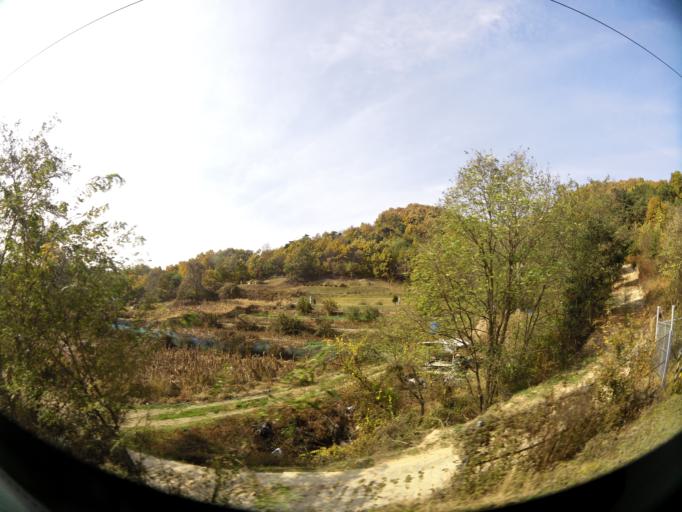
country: KR
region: Daejeon
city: Sintansin
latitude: 36.4700
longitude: 127.4209
